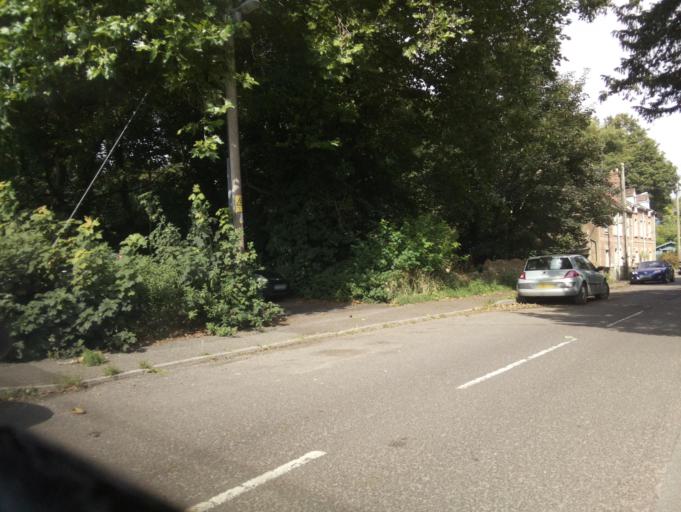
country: GB
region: England
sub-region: Somerset
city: Wincanton
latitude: 51.0580
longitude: -2.4134
